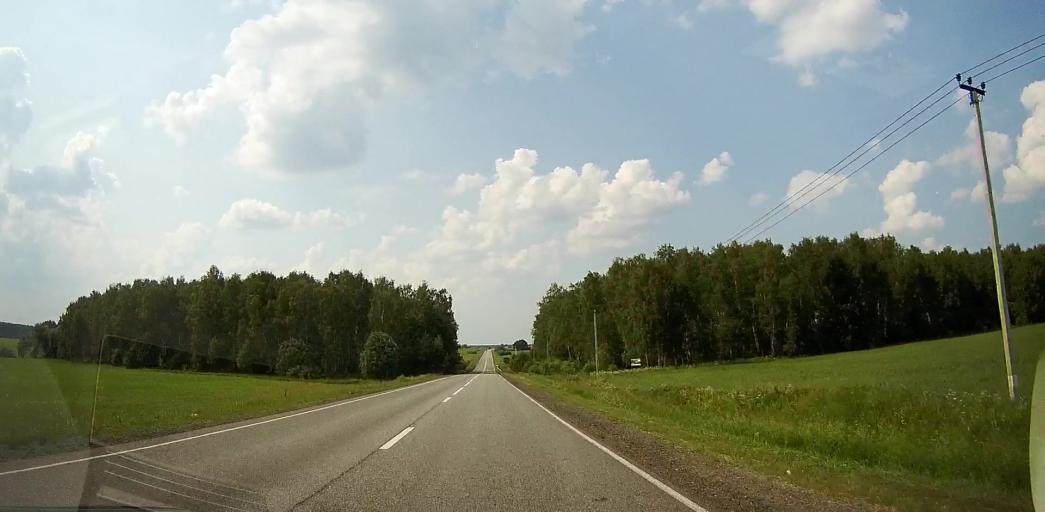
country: RU
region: Moskovskaya
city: Malino
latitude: 55.0275
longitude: 38.1701
